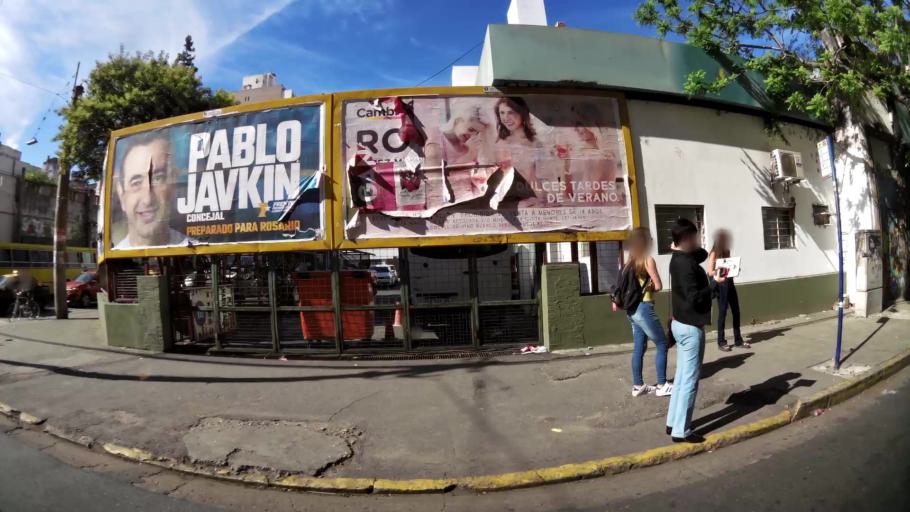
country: AR
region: Santa Fe
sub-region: Departamento de Rosario
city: Rosario
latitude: -32.9508
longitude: -60.6440
